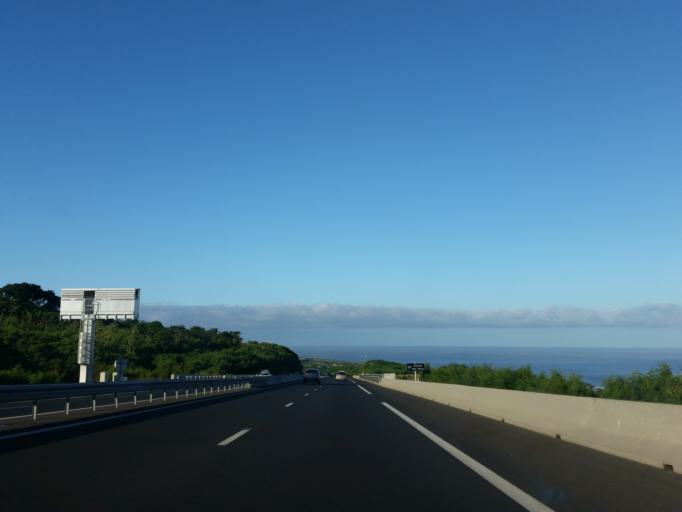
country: RE
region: Reunion
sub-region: Reunion
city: Saint-Leu
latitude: -21.1751
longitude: 55.2974
